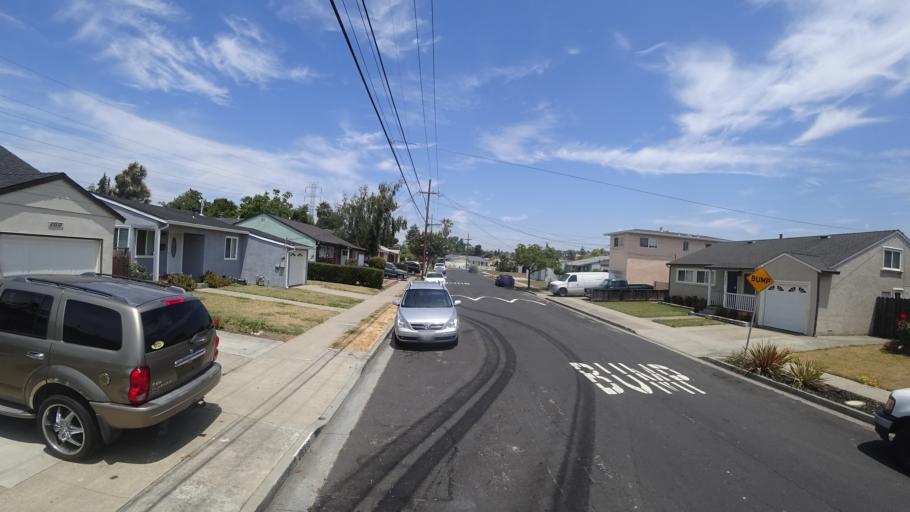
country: US
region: California
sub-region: Alameda County
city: Hayward
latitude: 37.6459
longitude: -122.0862
